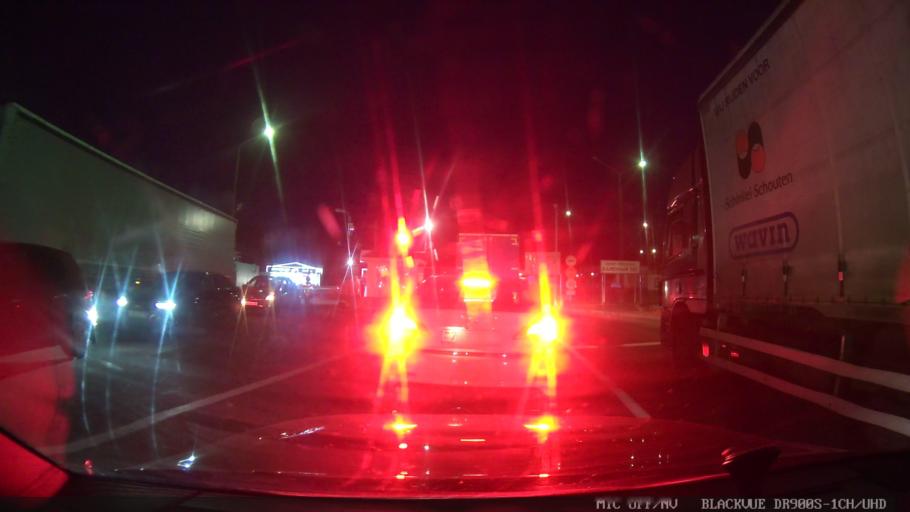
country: BY
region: Grodnenskaya
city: Astravyets
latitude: 54.5442
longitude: 25.6998
